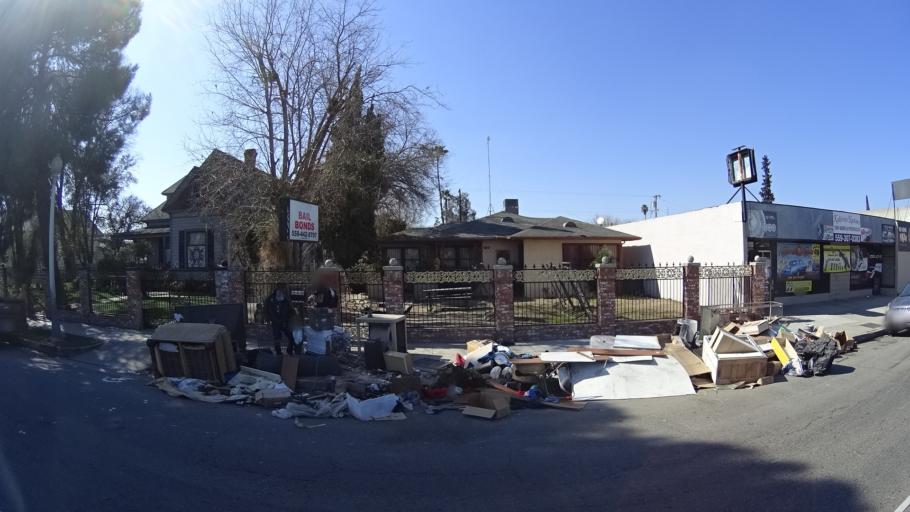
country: US
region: California
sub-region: Fresno County
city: Fresno
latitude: 36.7477
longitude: -119.7906
